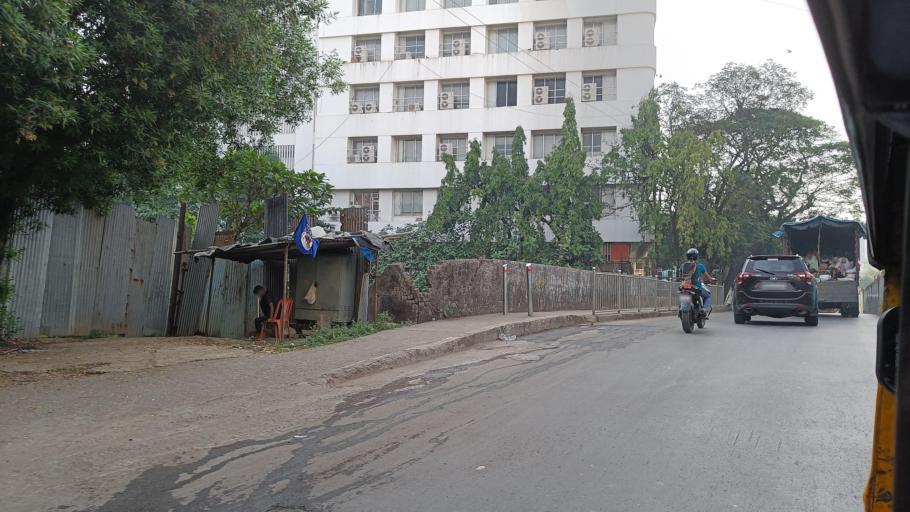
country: IN
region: Maharashtra
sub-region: Mumbai Suburban
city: Mumbai
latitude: 19.1105
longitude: 72.8373
